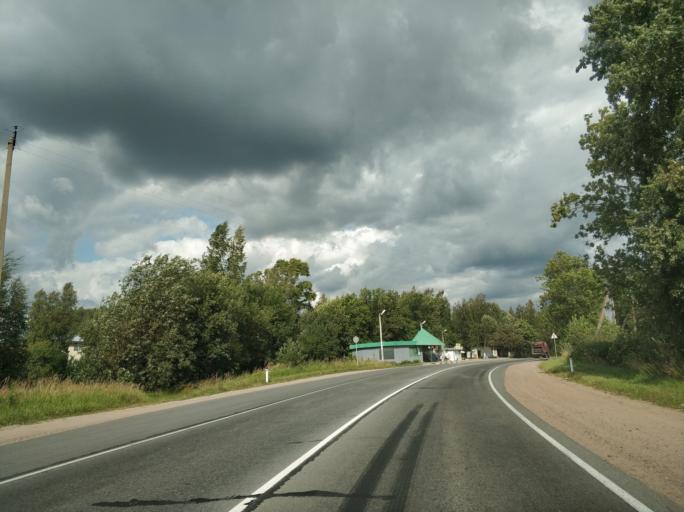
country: RU
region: Leningrad
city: Romanovka
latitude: 60.0677
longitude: 30.7411
